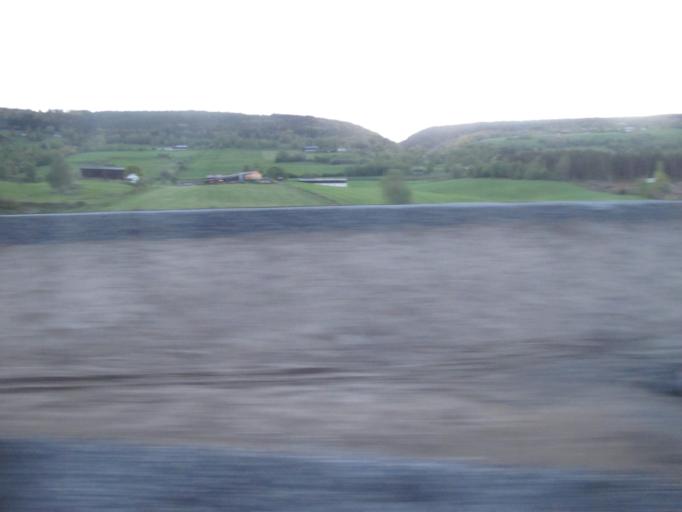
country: NO
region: Oppland
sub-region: Sor-Fron
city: Hundorp
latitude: 61.5690
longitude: 9.8991
